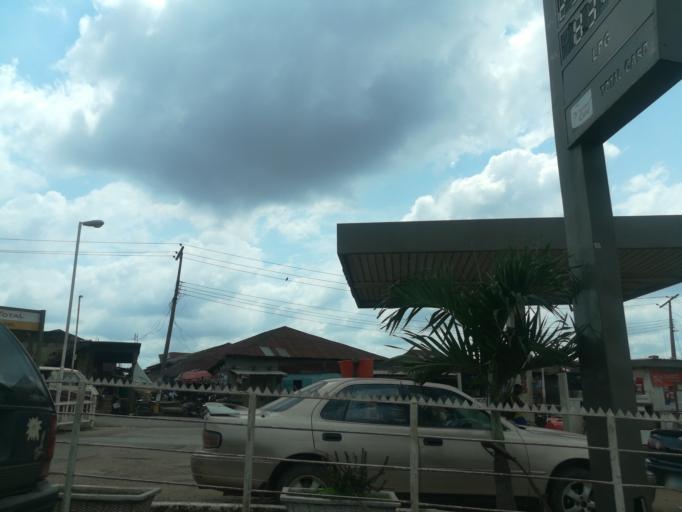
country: NG
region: Oyo
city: Ibadan
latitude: 7.3898
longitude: 3.9090
